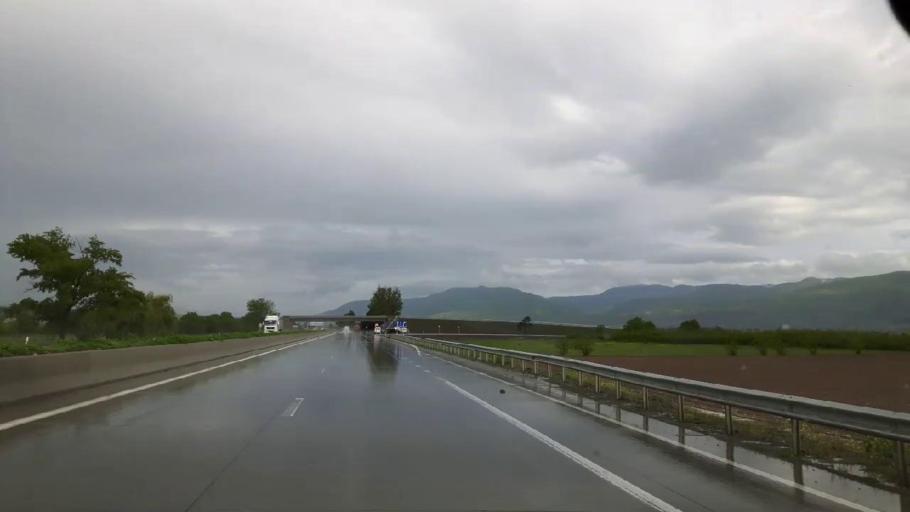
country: GE
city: Agara
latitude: 42.0329
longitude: 43.9464
